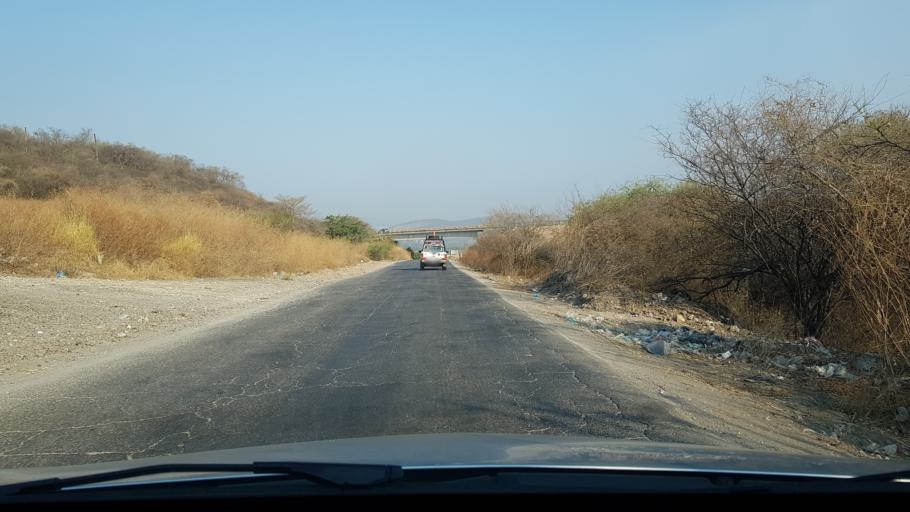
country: MX
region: Morelos
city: Tlaltizapan
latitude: 18.6775
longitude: -99.0792
